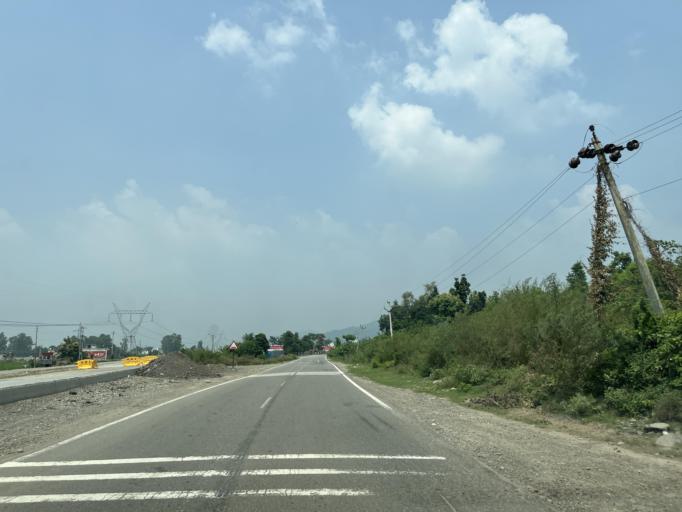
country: IN
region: Uttarakhand
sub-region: Haridwar
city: Haridwar
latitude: 29.8608
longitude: 78.1850
